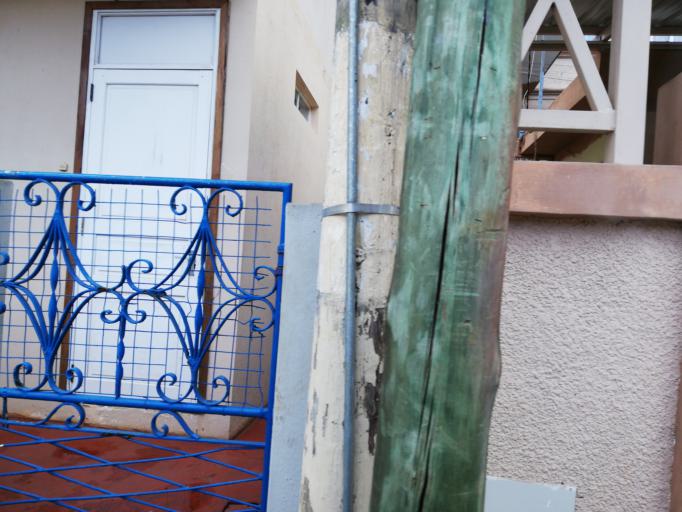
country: MU
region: Black River
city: Petite Riviere
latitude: -20.2133
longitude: 57.4655
